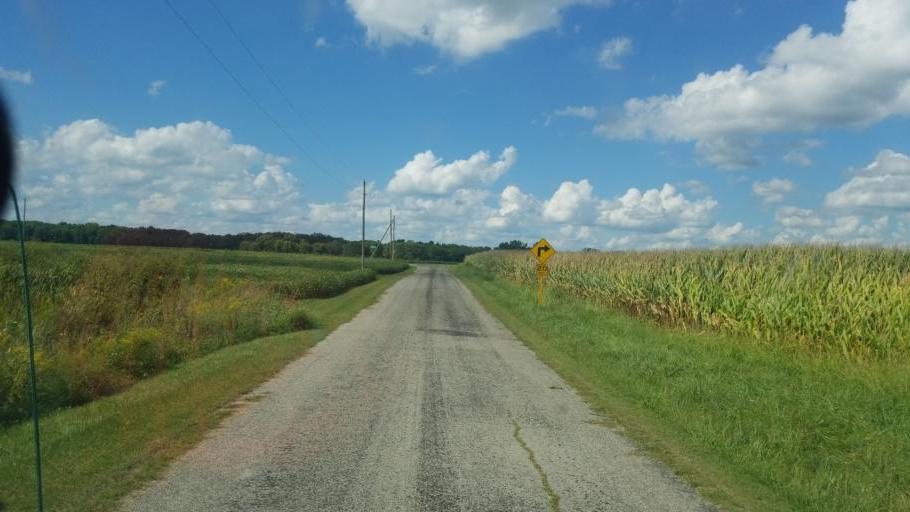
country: US
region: Ohio
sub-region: Union County
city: Richwood
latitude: 40.4654
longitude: -83.3435
